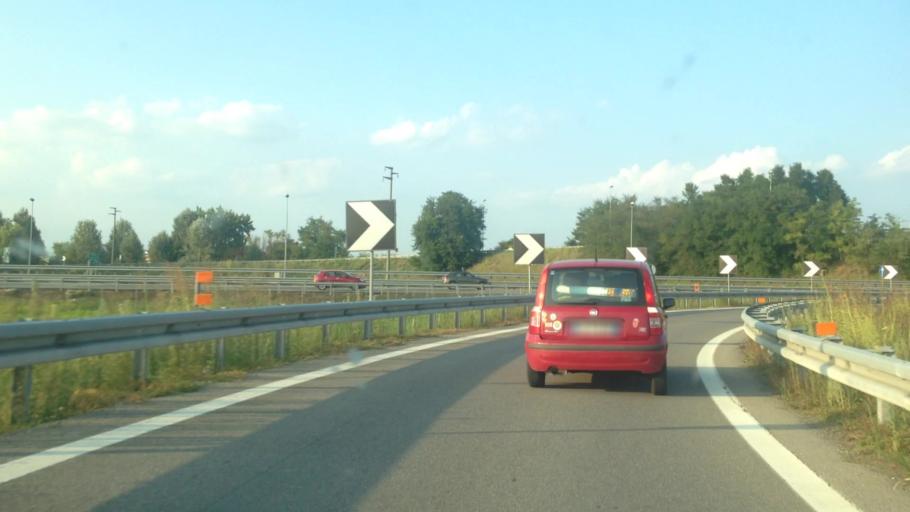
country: IT
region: Piedmont
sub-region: Provincia di Asti
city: Villanova d'Asti
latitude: 44.9531
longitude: 7.9148
